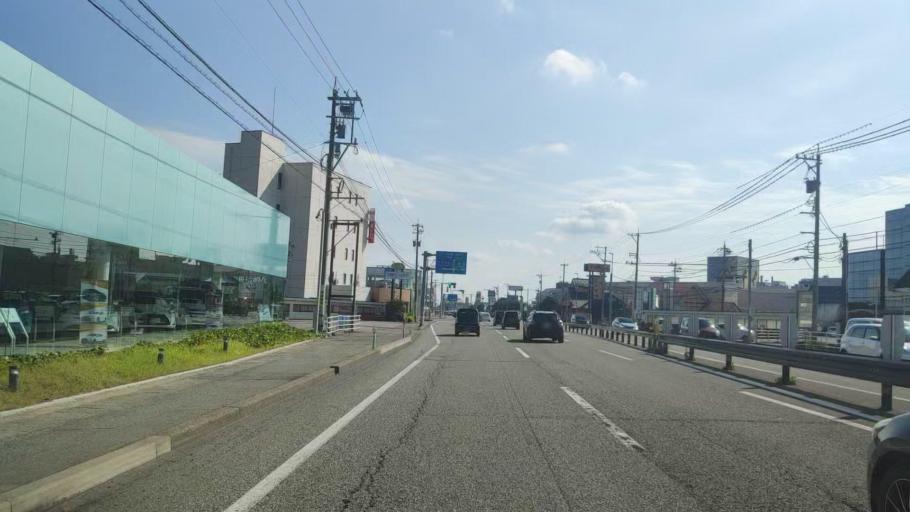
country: JP
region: Ishikawa
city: Matsuto
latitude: 36.5151
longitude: 136.5741
